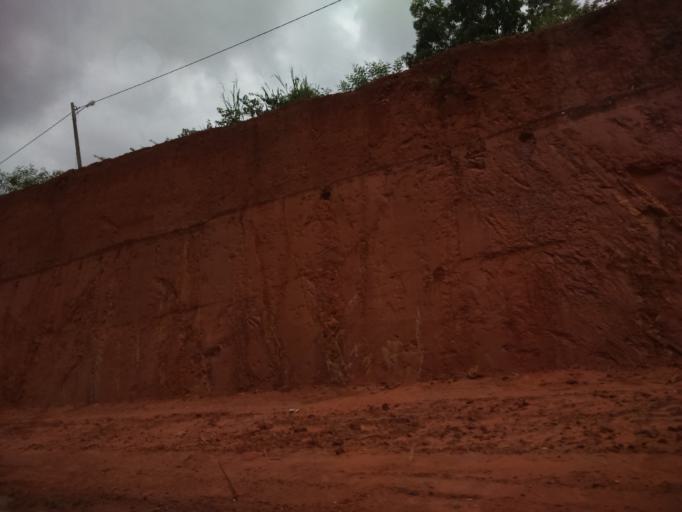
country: CI
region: Moyen-Comoe
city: Abengourou
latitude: 6.6264
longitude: -3.7110
